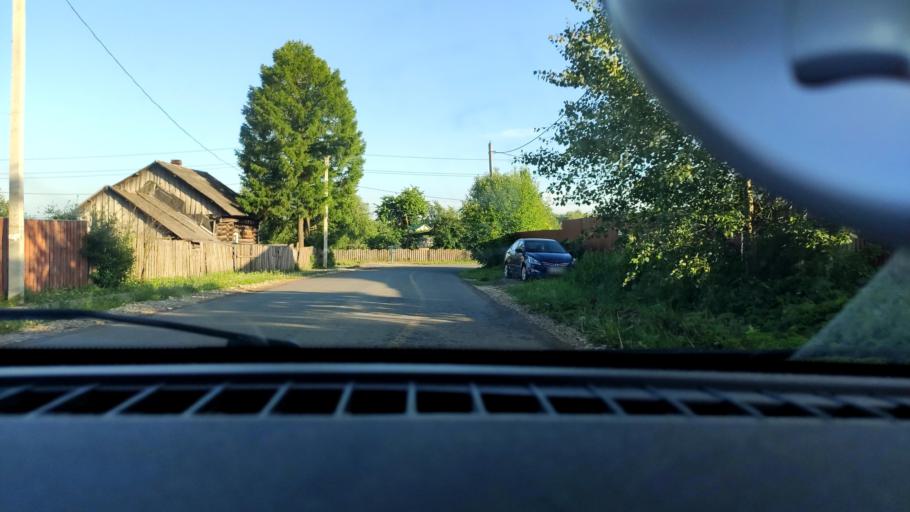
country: RU
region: Perm
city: Novyye Lyady
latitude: 58.0551
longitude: 56.6012
